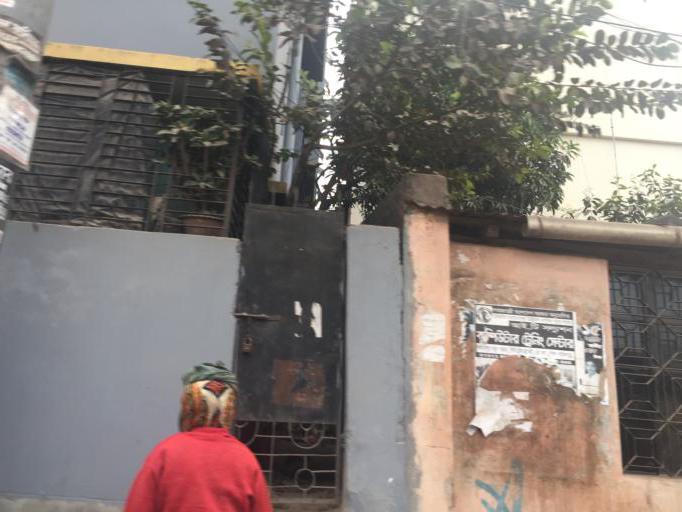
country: BD
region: Dhaka
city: Azimpur
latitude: 23.7876
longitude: 90.3598
